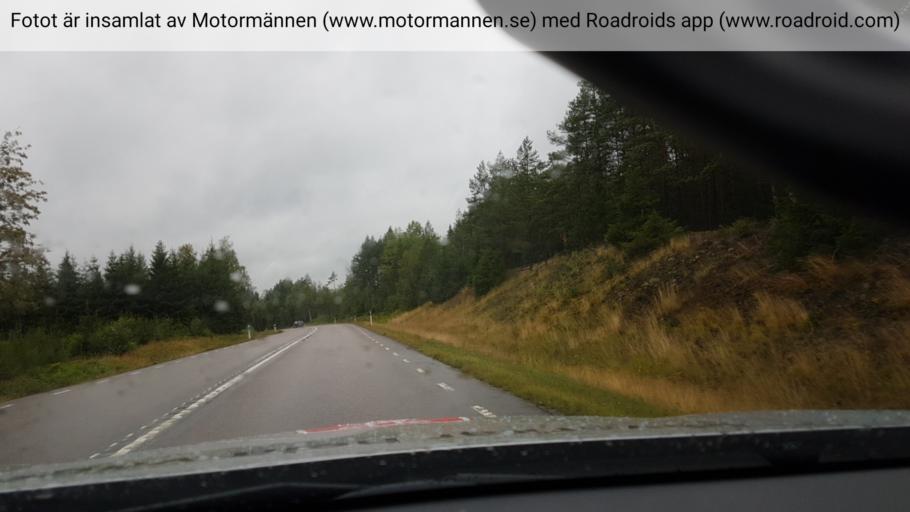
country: SE
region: Vaestra Goetaland
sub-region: Dals-Ed Kommun
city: Ed
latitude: 58.9298
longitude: 12.0401
